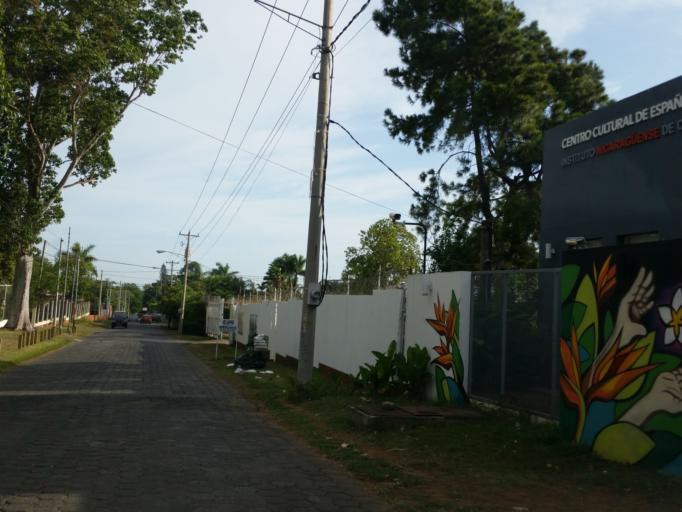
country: NI
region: Managua
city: Managua
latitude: 12.0961
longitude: -86.2332
